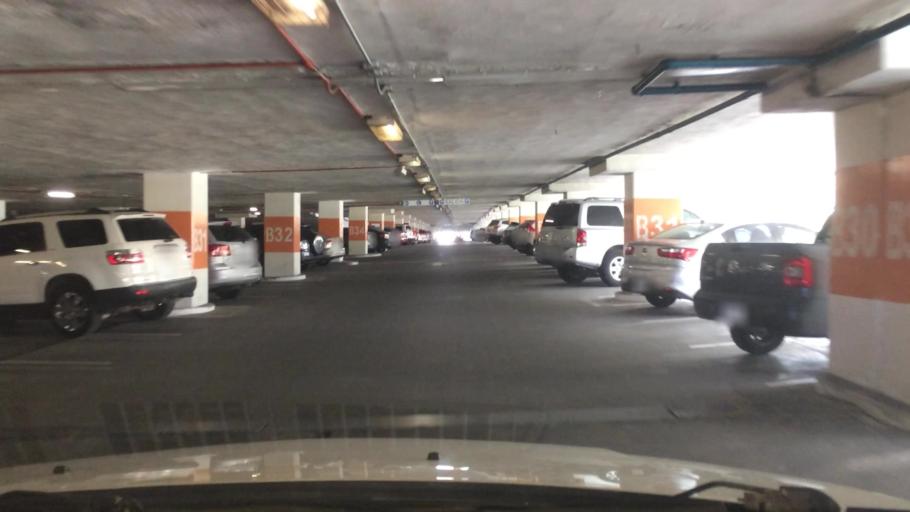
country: MX
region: Mexico City
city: Tlalpan
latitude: 19.3056
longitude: -99.1905
